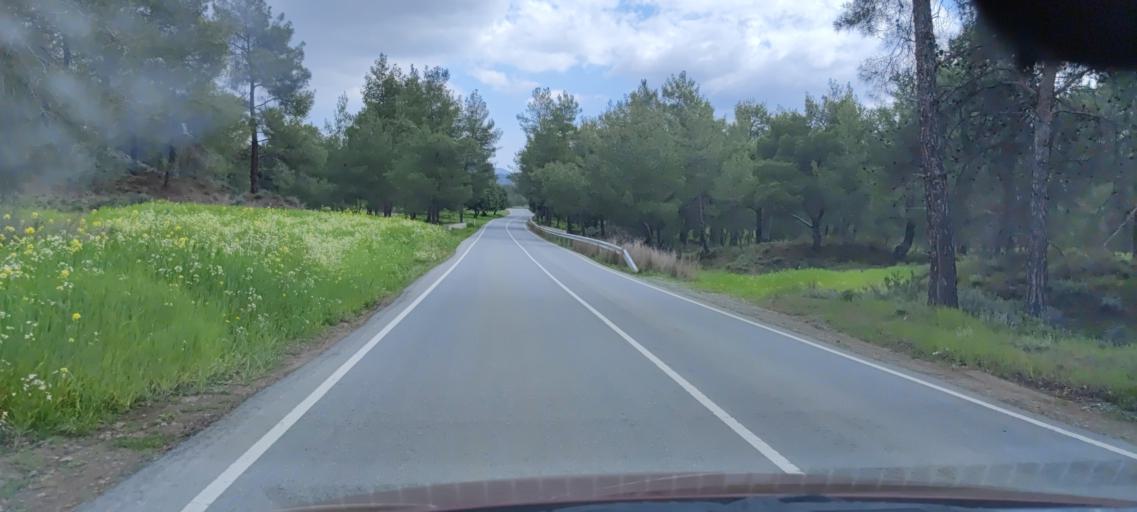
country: CY
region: Larnaka
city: Kornos
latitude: 34.9196
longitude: 33.3526
